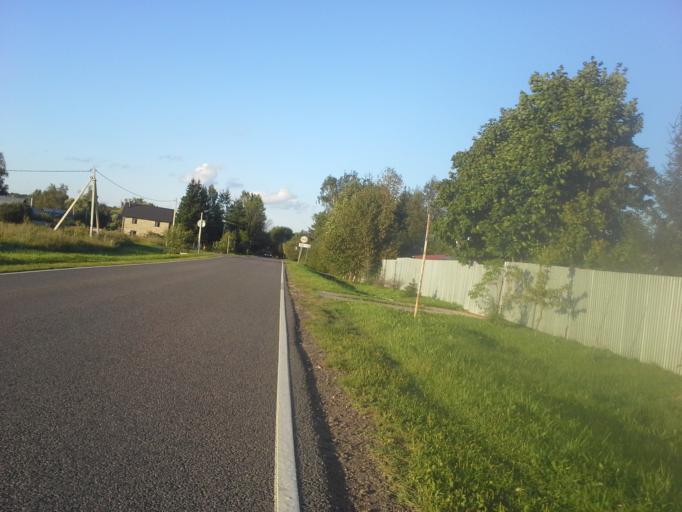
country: RU
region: Moskovskaya
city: Kievskij
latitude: 55.4701
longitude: 36.8977
